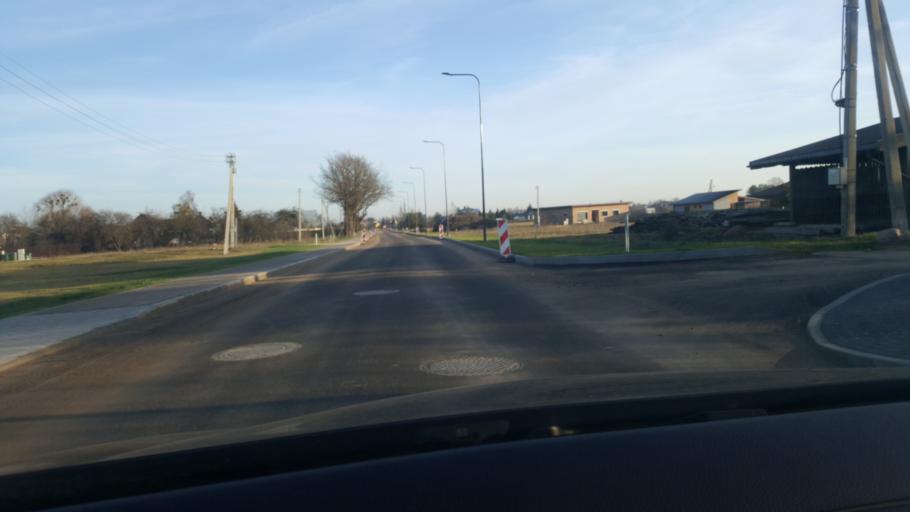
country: LT
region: Kauno apskritis
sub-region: Kauno rajonas
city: Mastaiciai
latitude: 54.8559
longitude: 23.8520
